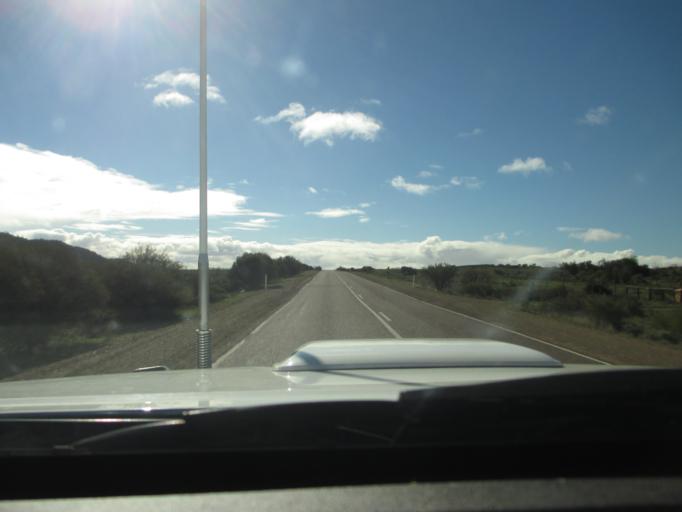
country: AU
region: South Australia
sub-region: Flinders Ranges
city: Quorn
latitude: -31.9371
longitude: 138.4091
